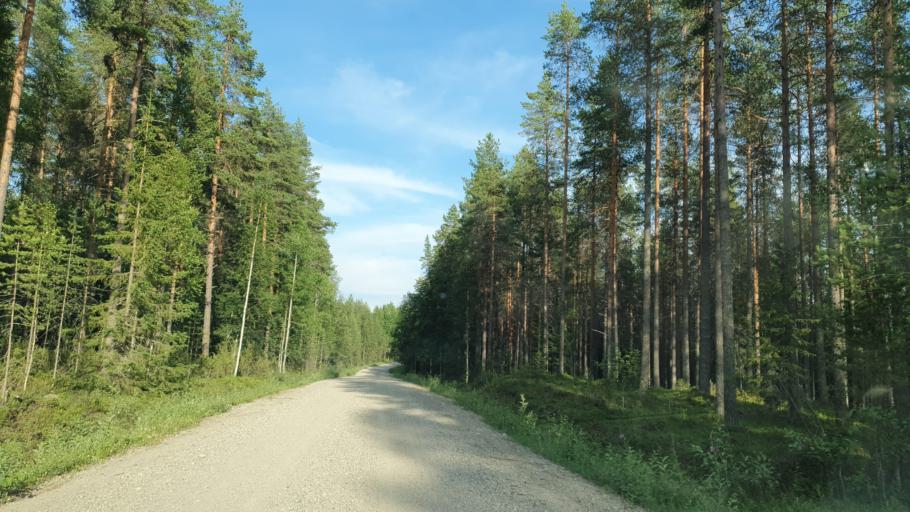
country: FI
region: Kainuu
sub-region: Kehys-Kainuu
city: Kuhmo
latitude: 64.3139
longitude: 29.5762
